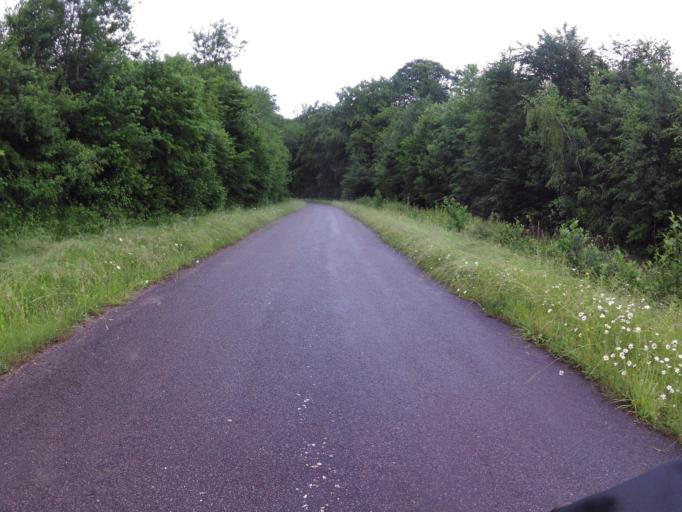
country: FR
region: Champagne-Ardenne
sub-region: Departement de la Marne
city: Sermaize-les-Bains
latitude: 48.7515
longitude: 4.9635
